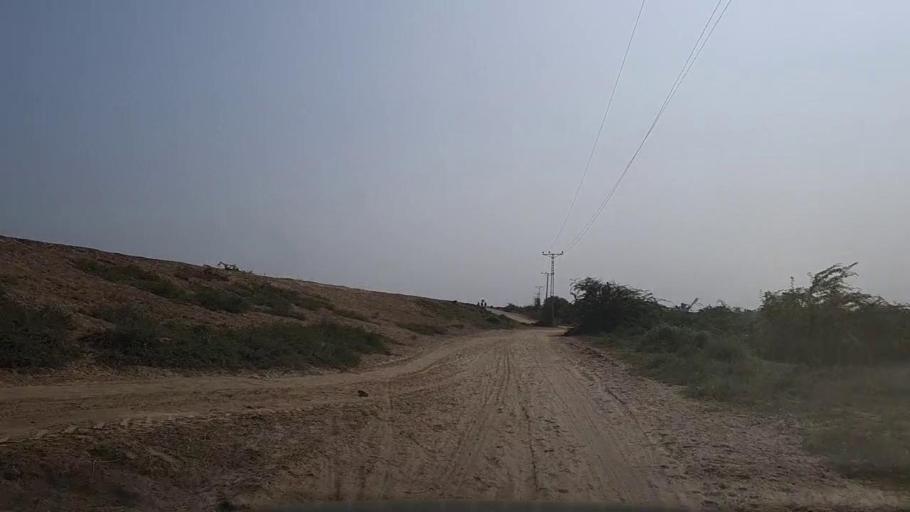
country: PK
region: Sindh
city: Chuhar Jamali
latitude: 24.5503
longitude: 67.9188
